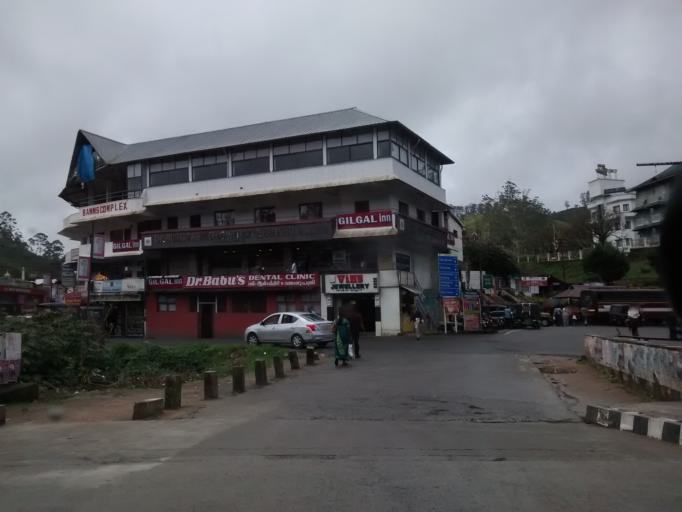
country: IN
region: Kerala
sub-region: Idukki
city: Munnar
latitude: 10.0859
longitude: 77.0608
